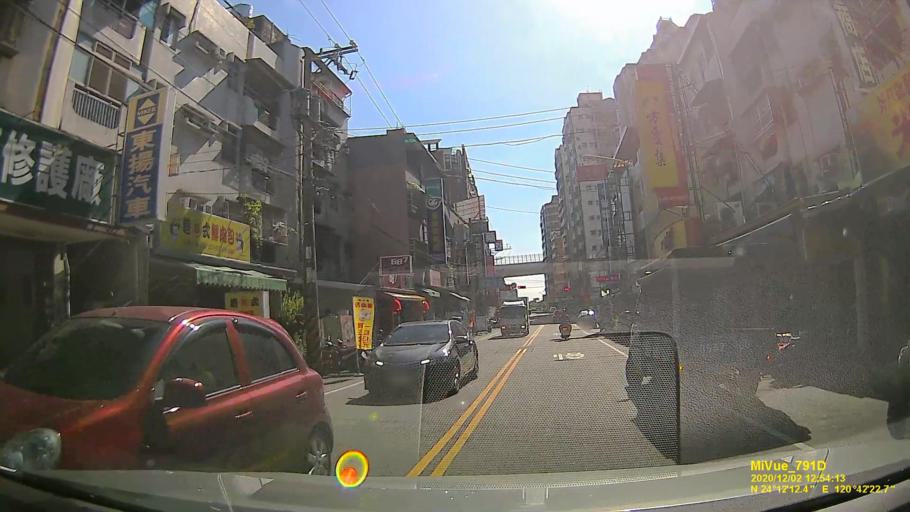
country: TW
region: Taiwan
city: Fengyuan
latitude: 24.2033
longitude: 120.7063
